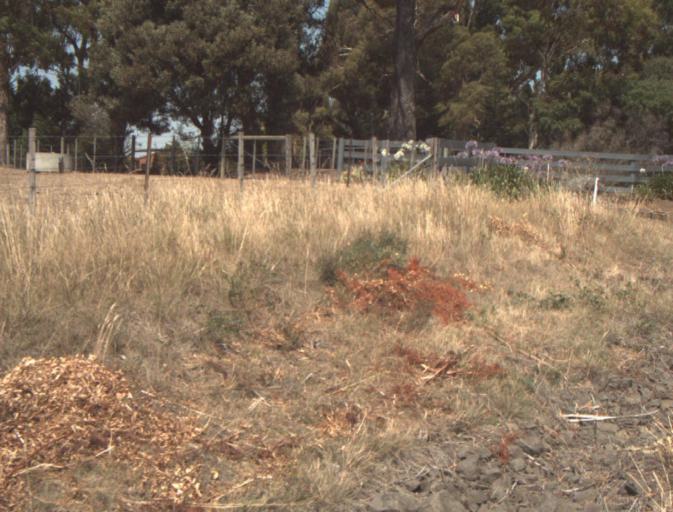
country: AU
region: Tasmania
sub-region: Launceston
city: Newstead
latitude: -41.4982
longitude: 147.2126
